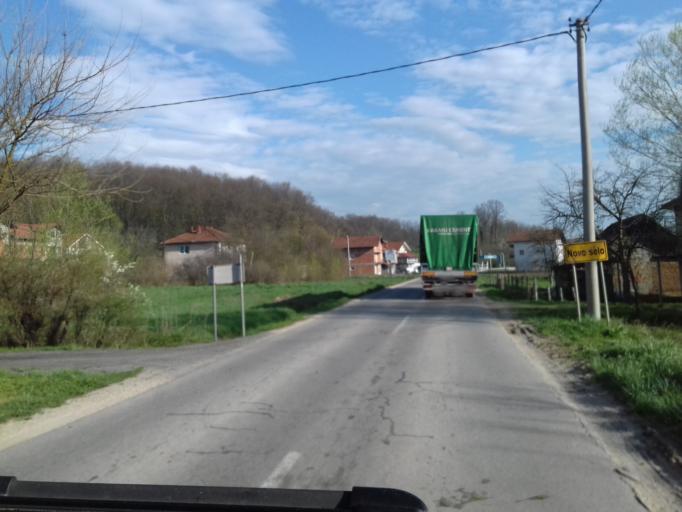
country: BA
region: Federation of Bosnia and Herzegovina
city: Tesanjka
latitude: 44.6553
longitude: 18.0164
